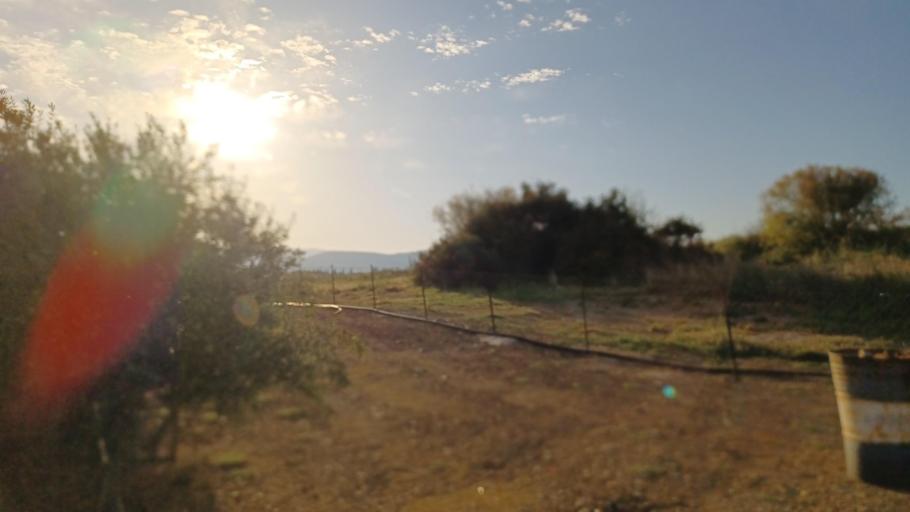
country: CY
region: Pafos
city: Polis
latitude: 35.0265
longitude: 32.3996
